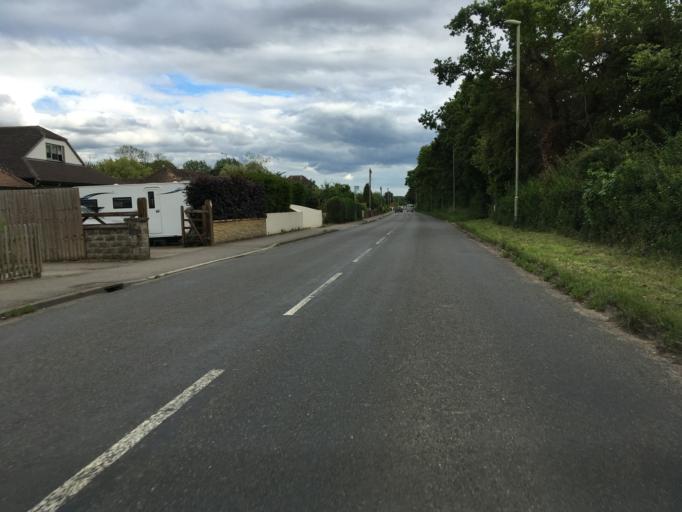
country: GB
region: England
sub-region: Oxfordshire
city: Boars Hill
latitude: 51.6949
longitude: -1.2979
